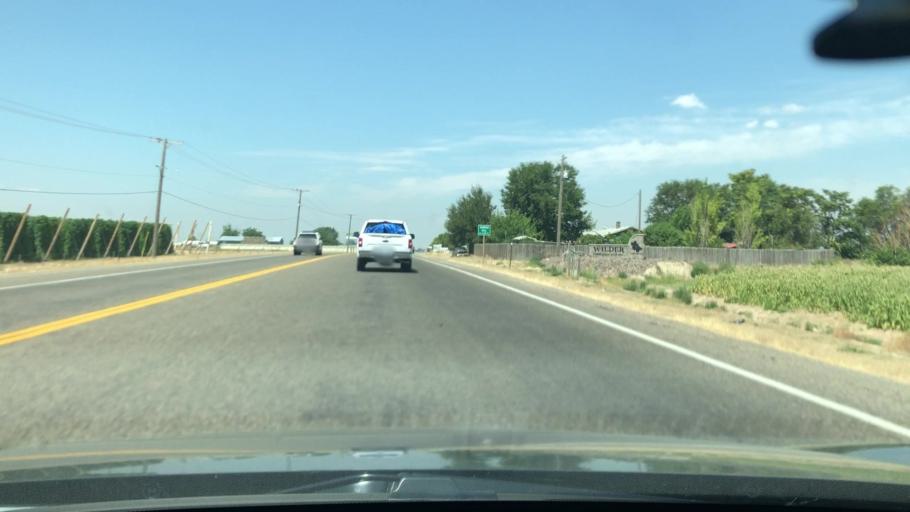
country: US
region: Idaho
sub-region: Canyon County
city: Wilder
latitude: 43.6629
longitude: -116.9119
